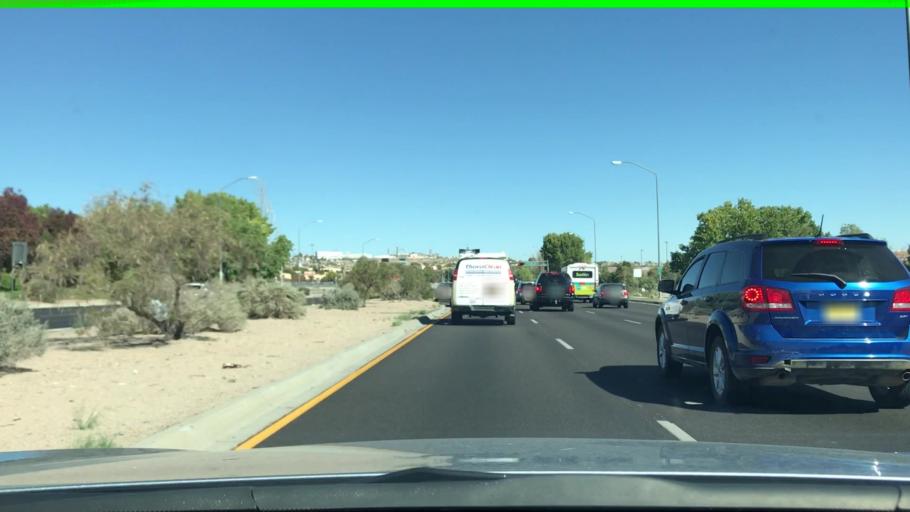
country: US
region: New Mexico
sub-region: Sandoval County
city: Rio Rancho
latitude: 35.1998
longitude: -106.6606
